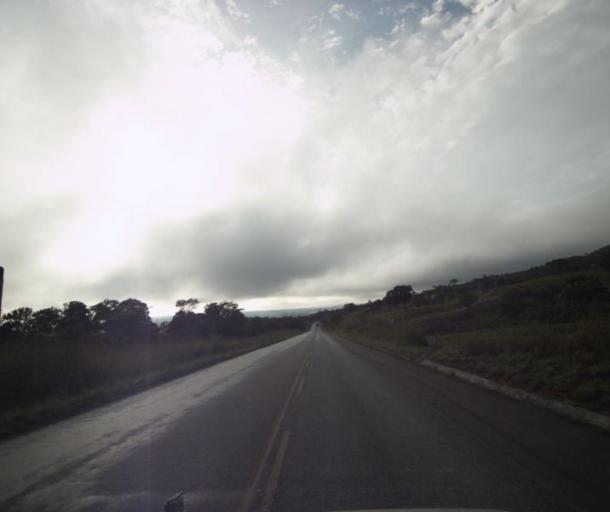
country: BR
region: Goias
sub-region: Pirenopolis
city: Pirenopolis
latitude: -15.7529
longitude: -48.7403
